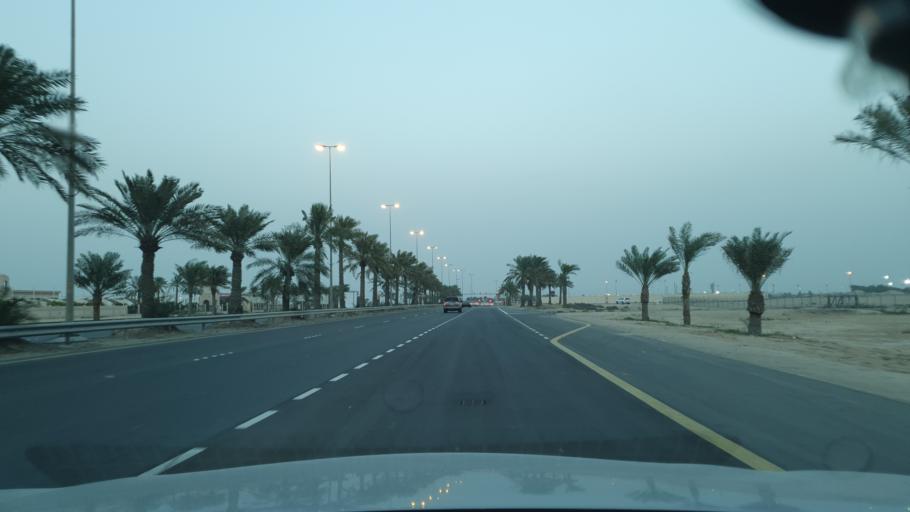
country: BH
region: Northern
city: Ar Rifa'
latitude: 26.0995
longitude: 50.5503
